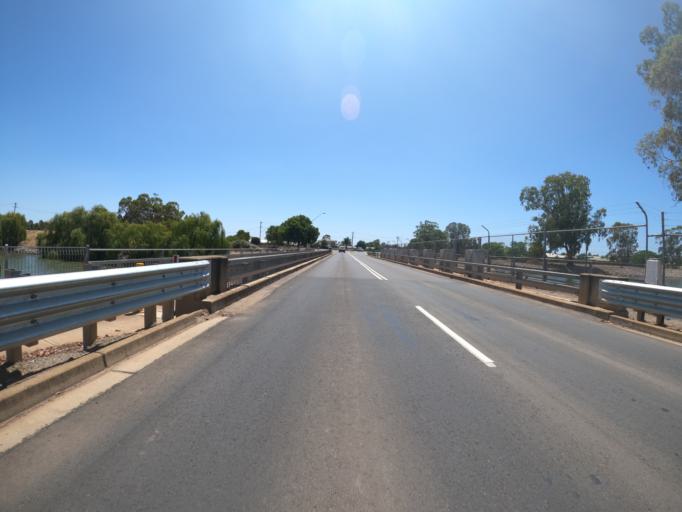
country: AU
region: New South Wales
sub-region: Corowa Shire
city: Mulwala
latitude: -35.9832
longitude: 146.0113
